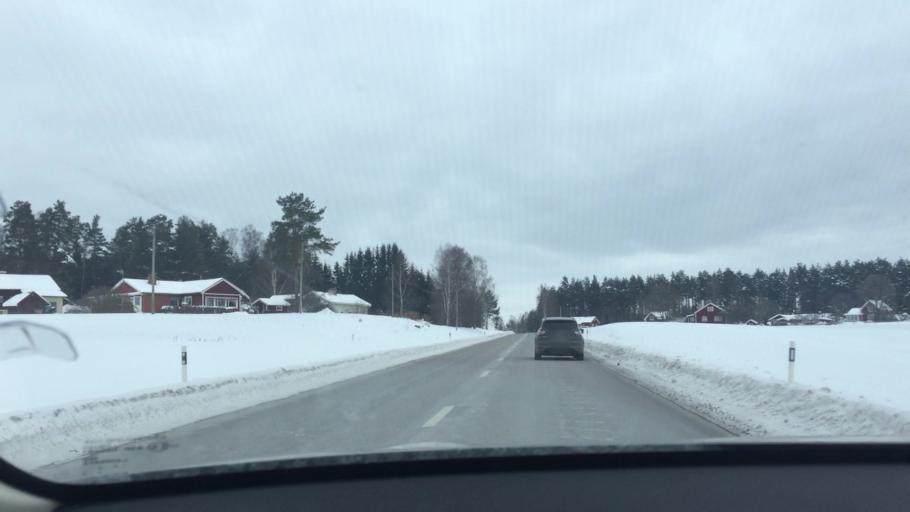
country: SE
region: Dalarna
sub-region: Faluns Kommun
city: Svardsjo
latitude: 60.6350
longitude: 15.8361
